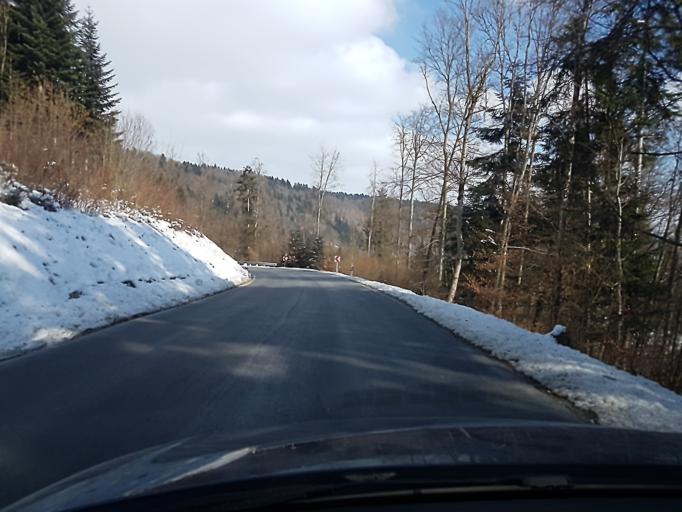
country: DE
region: Baden-Wuerttemberg
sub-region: Freiburg Region
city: Sulz am Neckar
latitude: 48.3466
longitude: 8.5860
